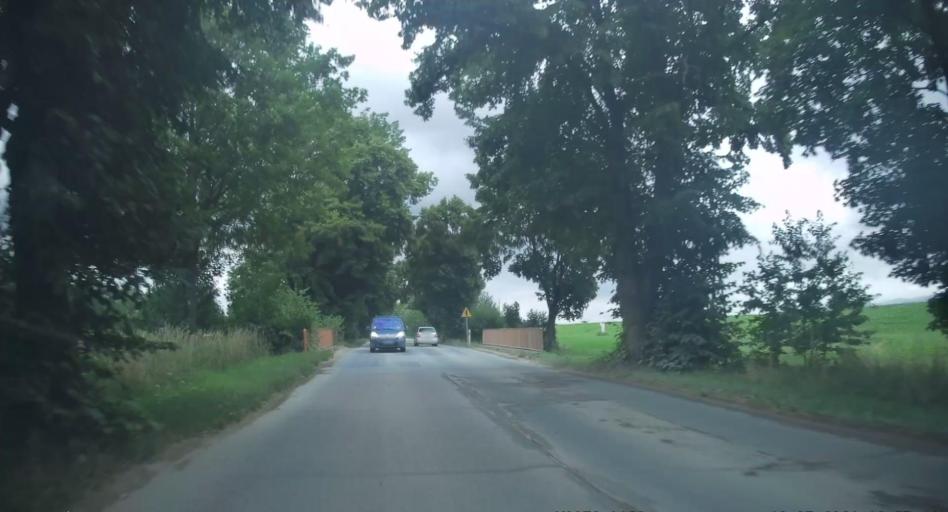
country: PL
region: Opole Voivodeship
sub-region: Powiat nyski
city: Kamienica
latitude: 50.4981
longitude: 16.9524
